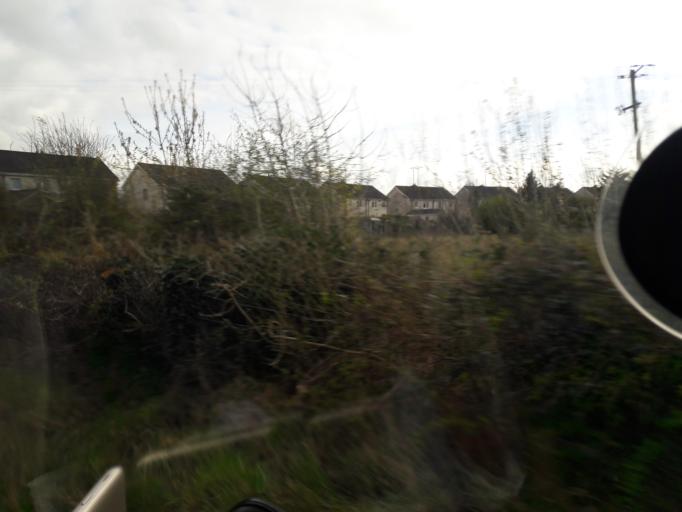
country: IE
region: Leinster
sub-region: An Iarmhi
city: An Muileann gCearr
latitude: 53.5161
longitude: -7.3275
